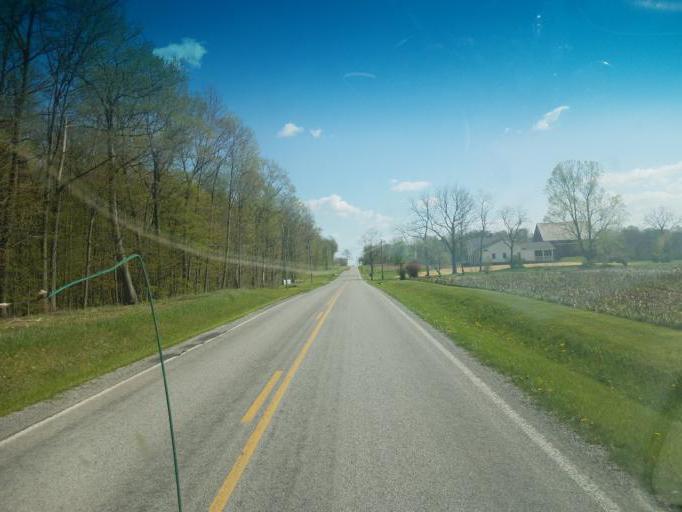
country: US
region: Ohio
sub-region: Medina County
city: Westfield Center
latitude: 40.9702
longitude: -81.9578
